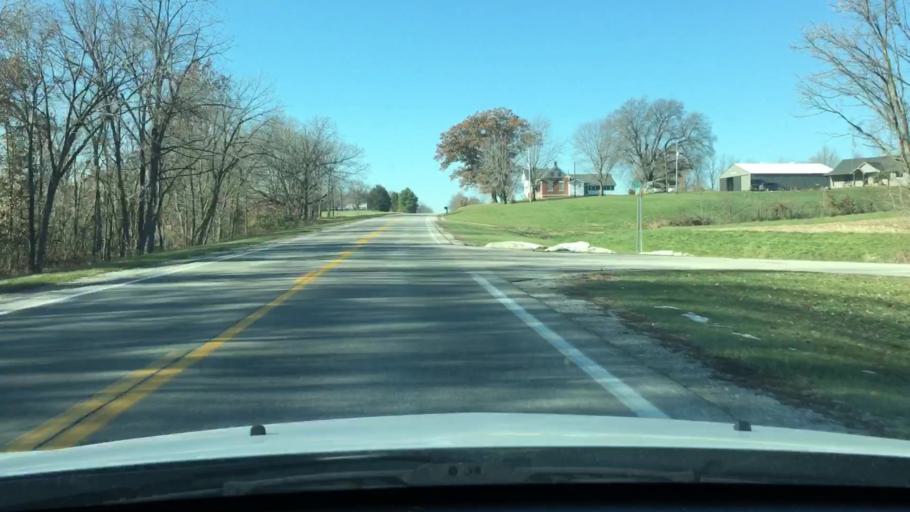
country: US
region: Illinois
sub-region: Pike County
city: Griggsville
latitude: 39.6192
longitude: -90.7027
